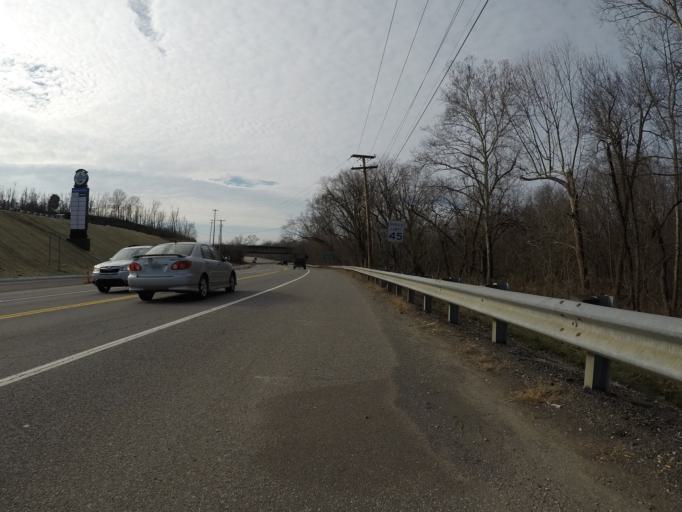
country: US
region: West Virginia
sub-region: Cabell County
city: Barboursville
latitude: 38.4161
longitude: -82.2917
